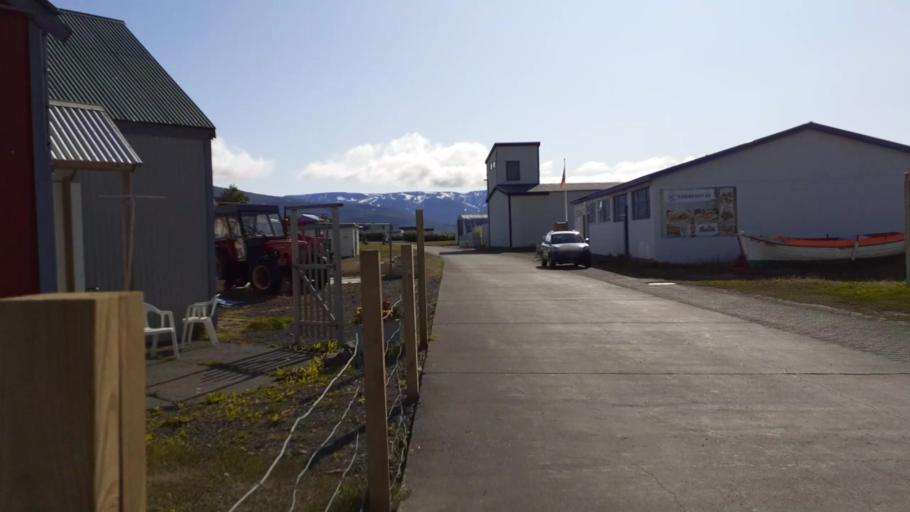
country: IS
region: Northeast
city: Dalvik
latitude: 65.9784
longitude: -18.3779
